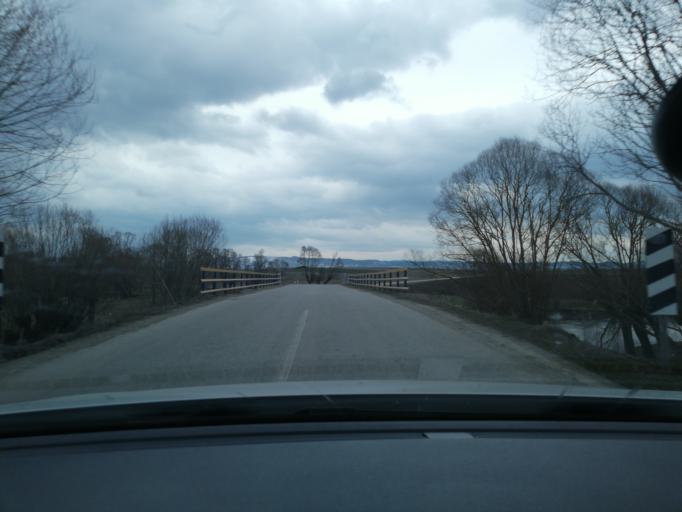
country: TR
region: Bolu
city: Gerede
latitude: 40.7279
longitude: 32.2206
